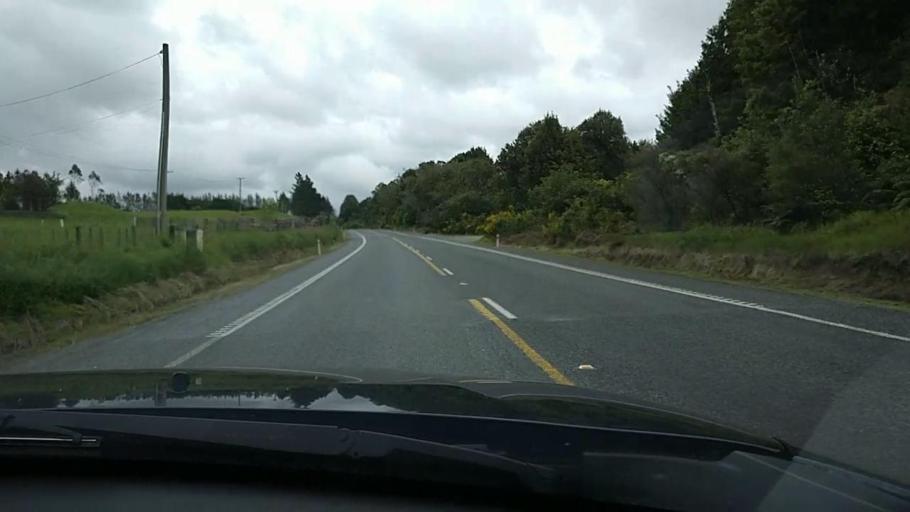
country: NZ
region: Bay of Plenty
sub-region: Rotorua District
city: Rotorua
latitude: -38.0674
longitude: 176.1082
